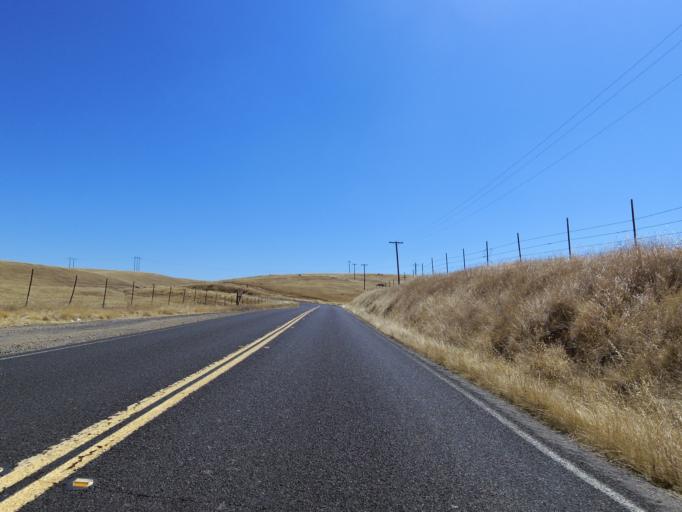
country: US
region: California
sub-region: Merced County
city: Planada
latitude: 37.4821
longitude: -120.2719
